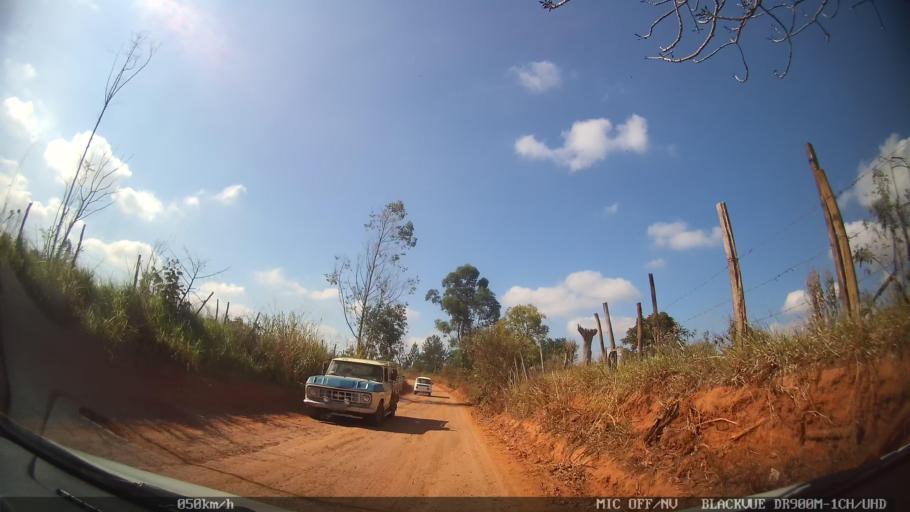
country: BR
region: Sao Paulo
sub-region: Indaiatuba
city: Indaiatuba
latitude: -22.9987
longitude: -47.2058
